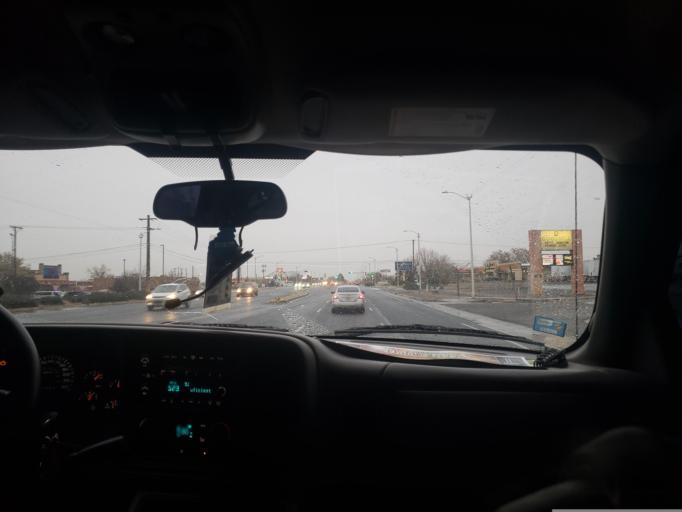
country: US
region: New Mexico
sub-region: Bernalillo County
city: North Valley
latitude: 35.1364
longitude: -106.5864
